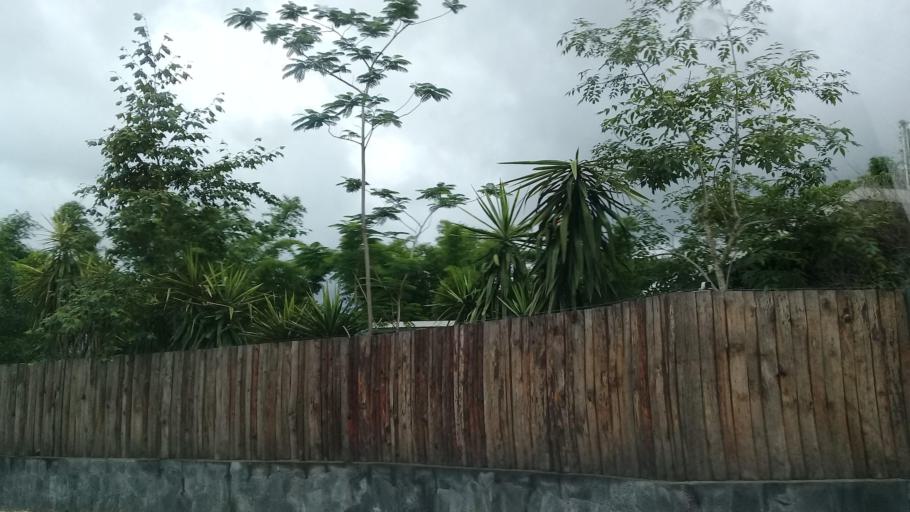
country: MX
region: Veracruz
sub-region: Emiliano Zapata
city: Jacarandas
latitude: 19.5083
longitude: -96.8439
